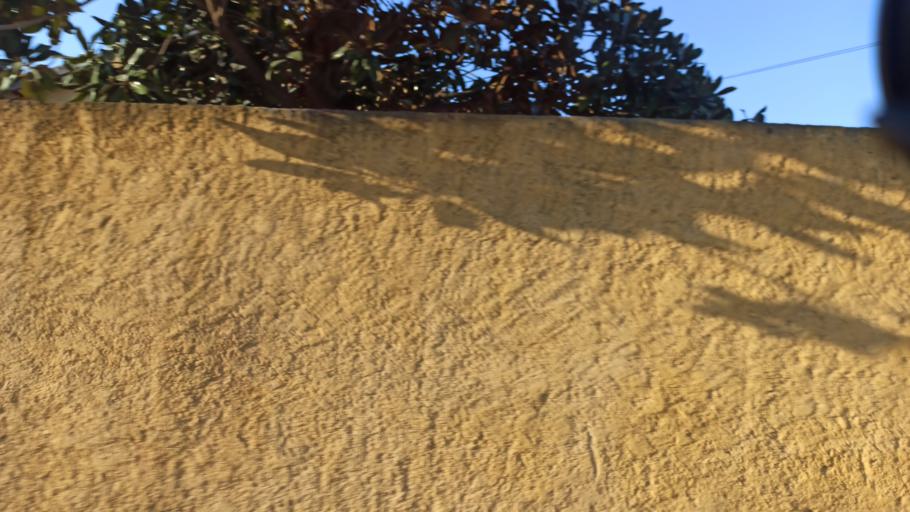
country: AL
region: Shkoder
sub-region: Rrethi i Shkodres
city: Shkoder
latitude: 42.0785
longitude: 19.4966
